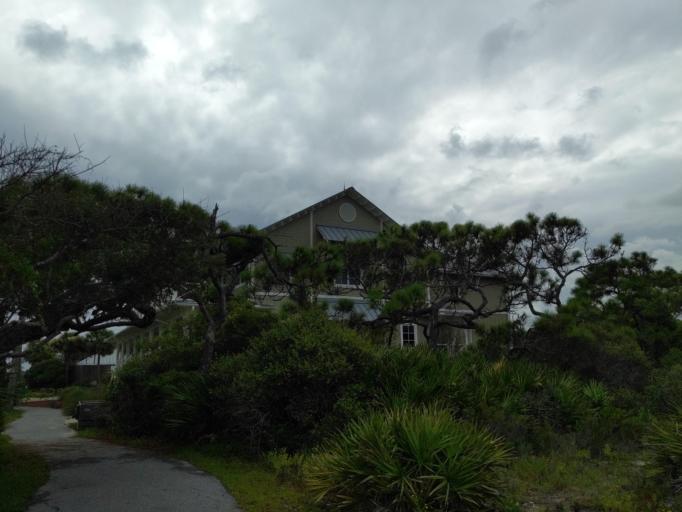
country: US
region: Florida
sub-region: Franklin County
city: Apalachicola
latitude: 29.6301
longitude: -84.9273
